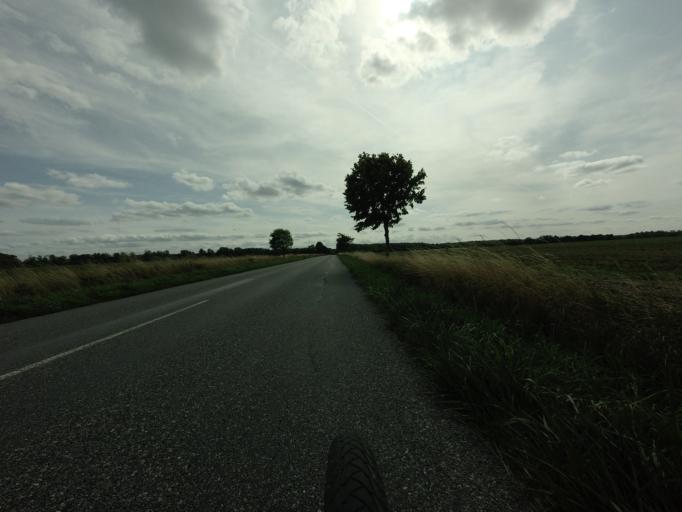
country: DK
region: Zealand
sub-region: Faxe Kommune
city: Fakse Ladeplads
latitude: 55.2456
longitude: 12.2195
